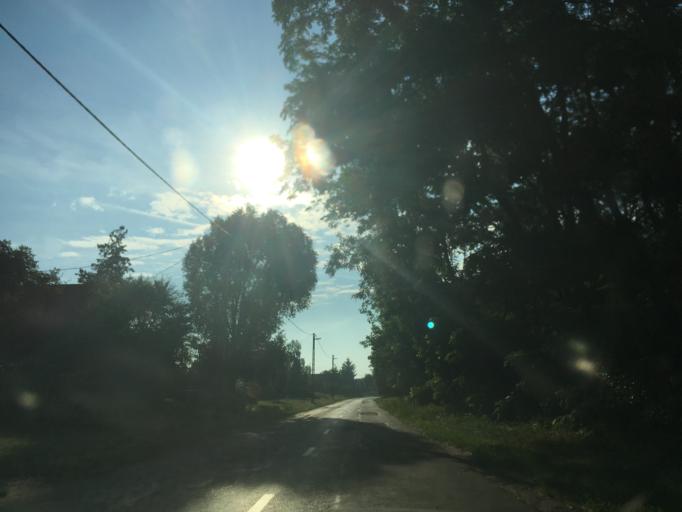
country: HU
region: Hajdu-Bihar
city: Hajdusamson
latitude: 47.5644
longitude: 21.7553
